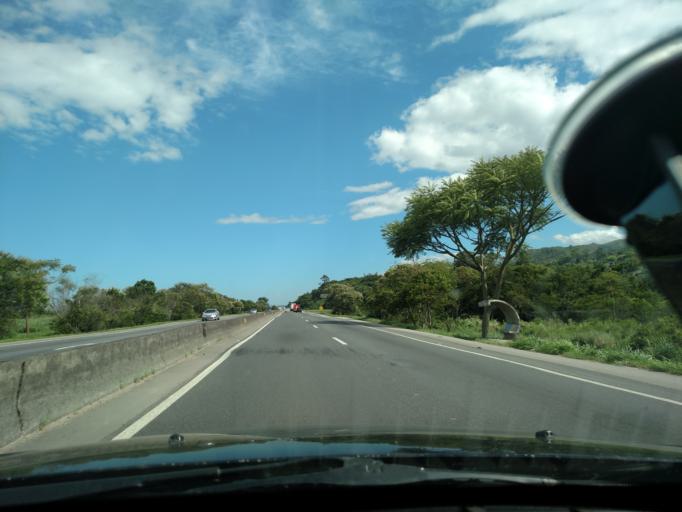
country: BR
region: Santa Catarina
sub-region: Biguacu
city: Biguacu
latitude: -27.4091
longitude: -48.6280
